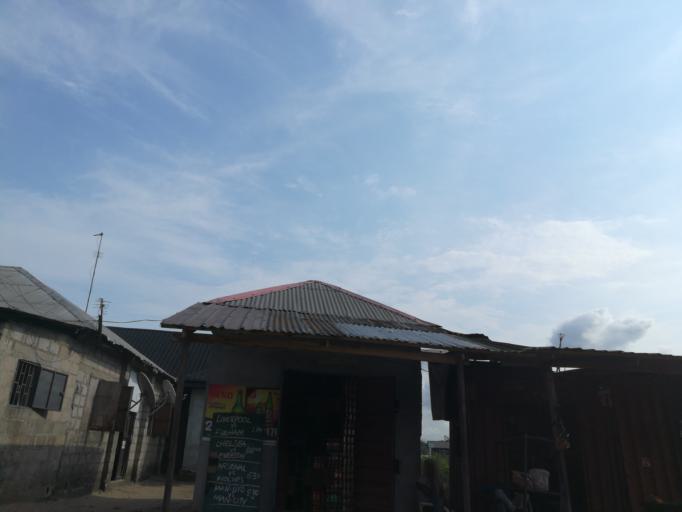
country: NG
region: Rivers
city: Okrika
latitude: 4.7455
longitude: 7.0887
